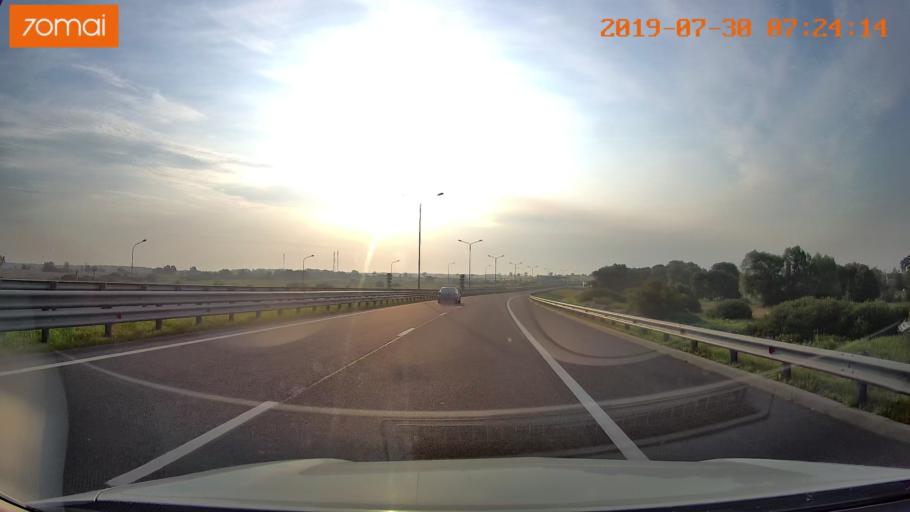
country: RU
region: Kaliningrad
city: Bol'shoe Isakovo
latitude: 54.6934
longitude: 20.8065
